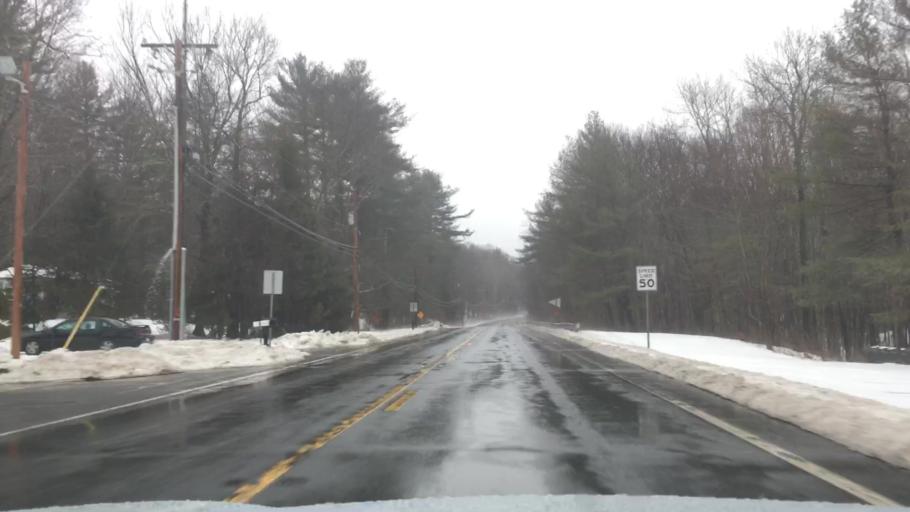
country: US
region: Massachusetts
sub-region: Hampshire County
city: Belchertown
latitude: 42.2962
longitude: -72.4069
